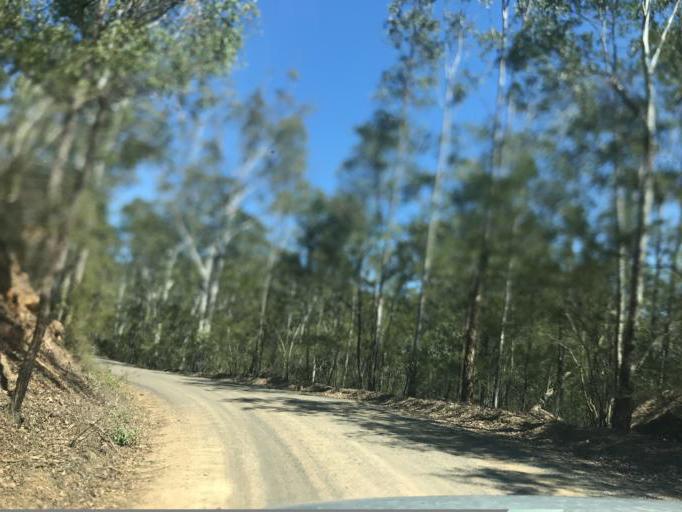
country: AU
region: New South Wales
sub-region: Wyong Shire
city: Little Jilliby
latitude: -33.1631
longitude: 151.0679
